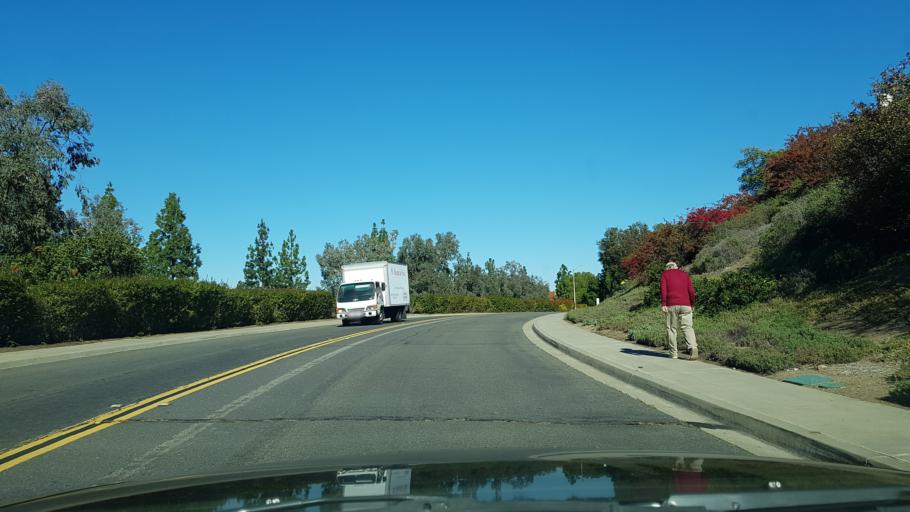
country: US
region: California
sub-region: San Diego County
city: Poway
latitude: 33.0340
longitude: -117.0749
